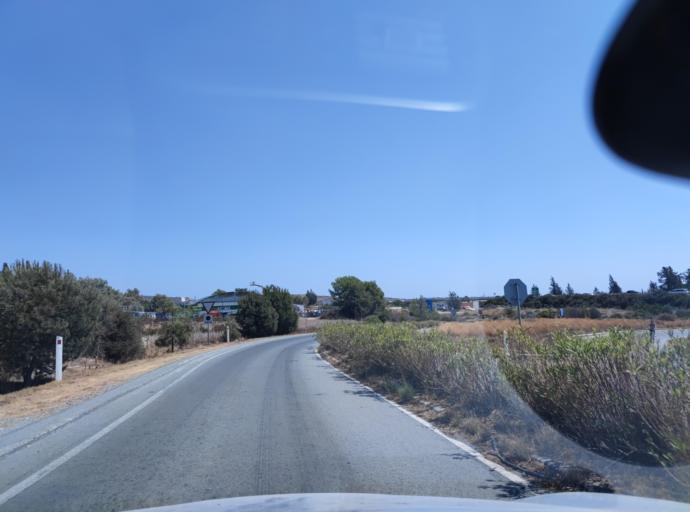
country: CY
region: Larnaka
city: Kofinou
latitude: 34.7572
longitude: 33.3174
